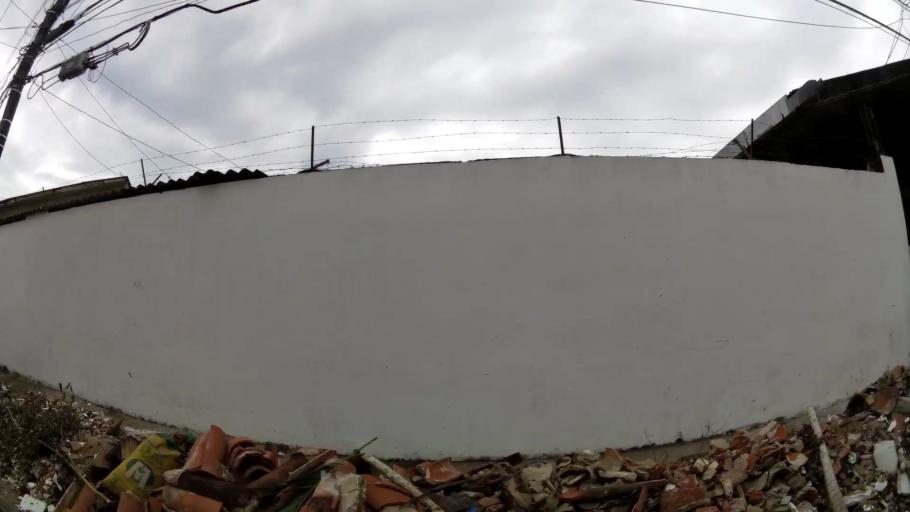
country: BO
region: Santa Cruz
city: Santa Cruz de la Sierra
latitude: -17.7743
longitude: -63.2046
